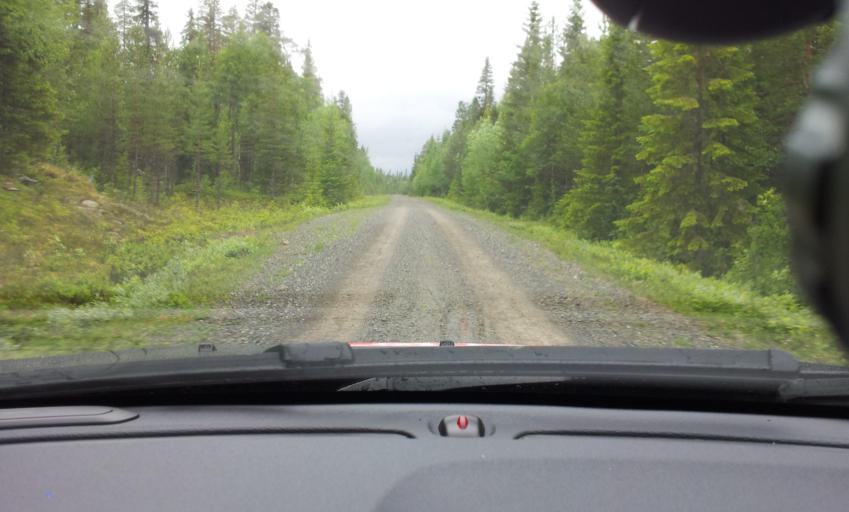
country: SE
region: Jaemtland
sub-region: Are Kommun
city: Jarpen
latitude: 63.2080
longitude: 13.3180
